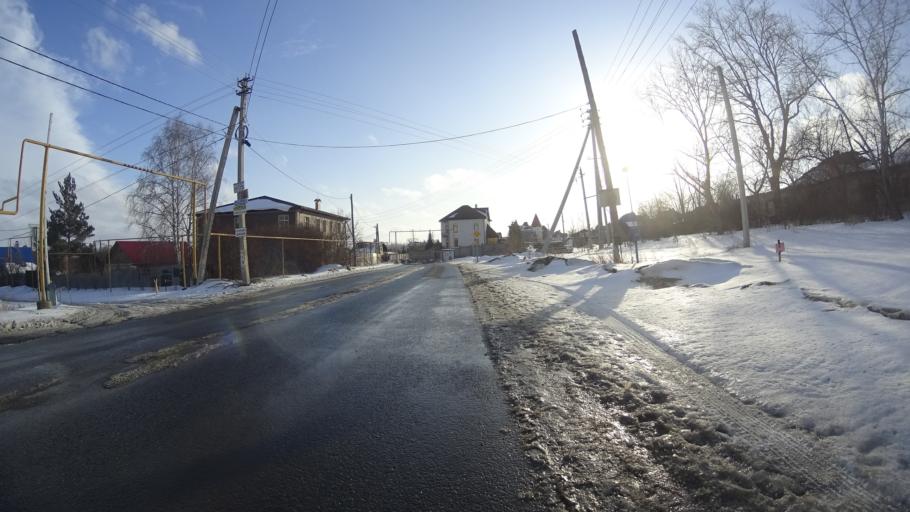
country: RU
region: Chelyabinsk
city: Sargazy
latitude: 55.1142
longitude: 61.2821
